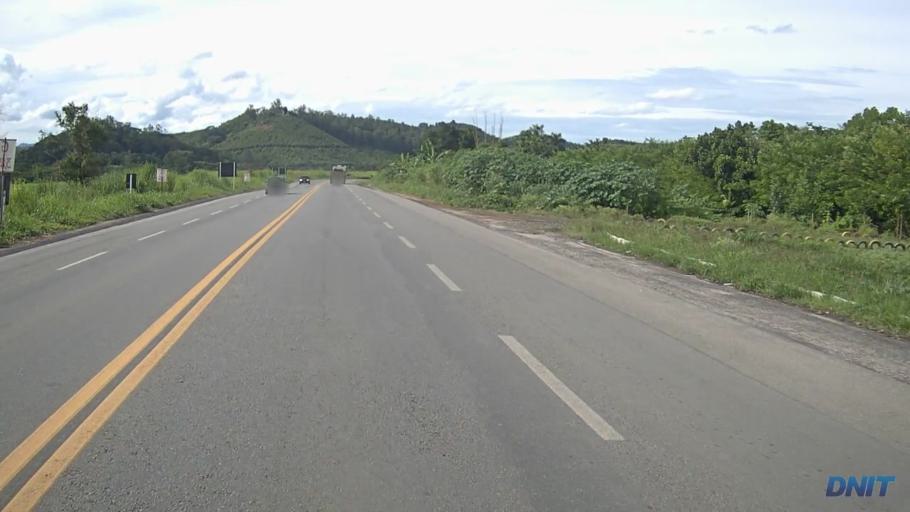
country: BR
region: Minas Gerais
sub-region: Belo Oriente
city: Belo Oriente
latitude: -19.2828
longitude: -42.3569
